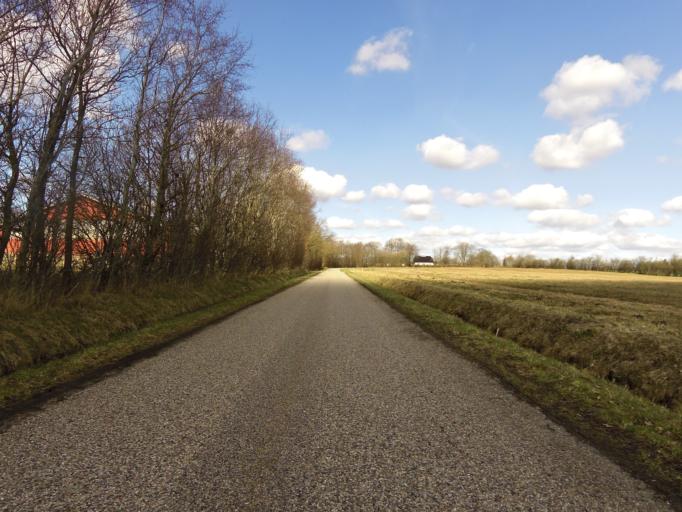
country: DK
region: South Denmark
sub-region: Tonder Kommune
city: Toftlund
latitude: 55.1792
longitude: 9.0885
